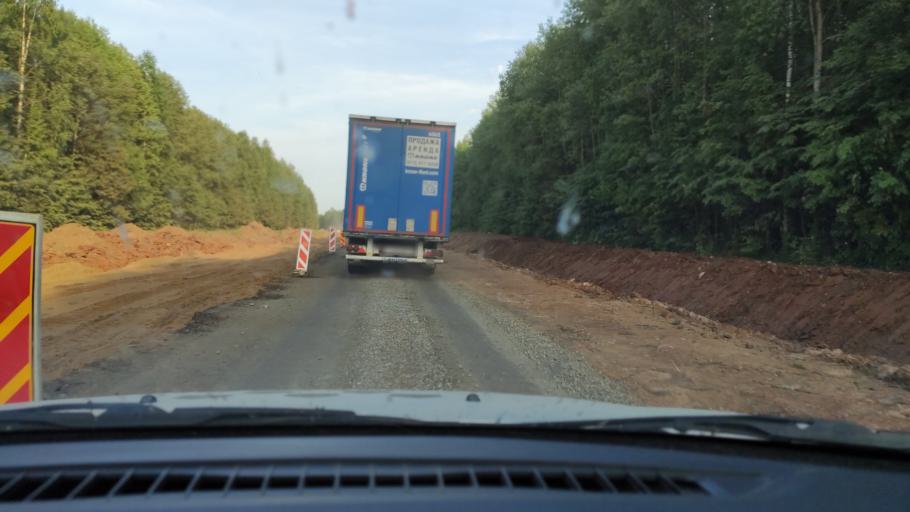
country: RU
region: Perm
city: Siva
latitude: 58.4876
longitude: 54.3654
